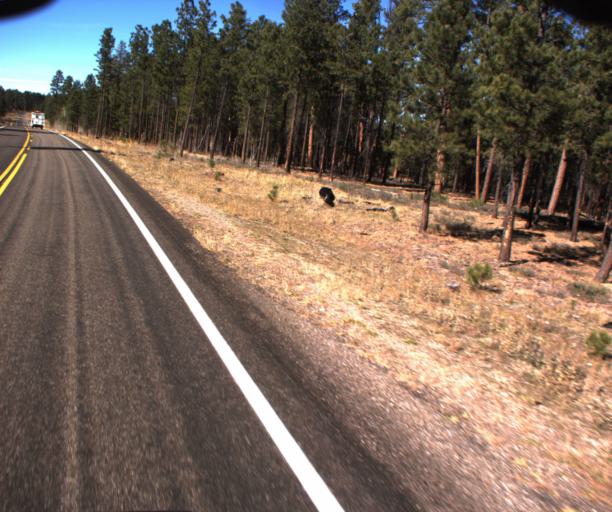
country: US
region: Arizona
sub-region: Coconino County
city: Fredonia
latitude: 36.6790
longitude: -112.2113
